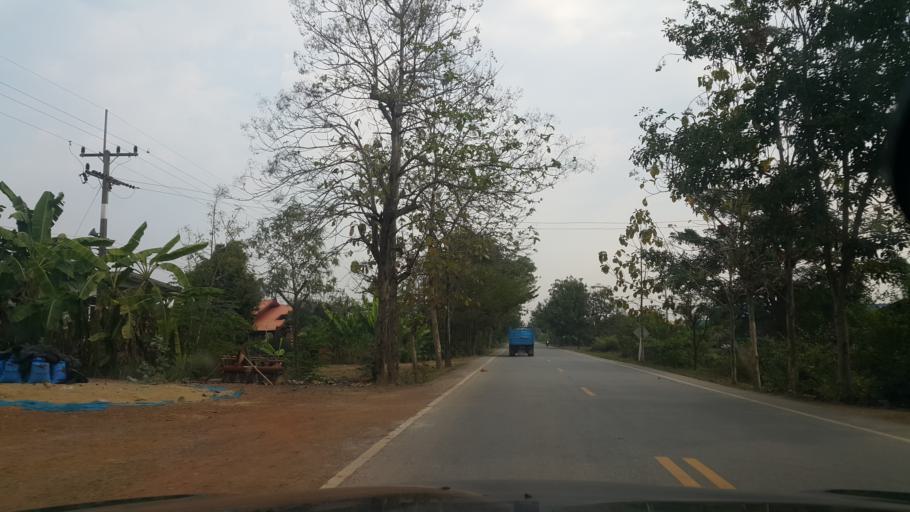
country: TH
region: Sukhothai
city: Si Samrong
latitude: 17.1726
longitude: 99.7324
